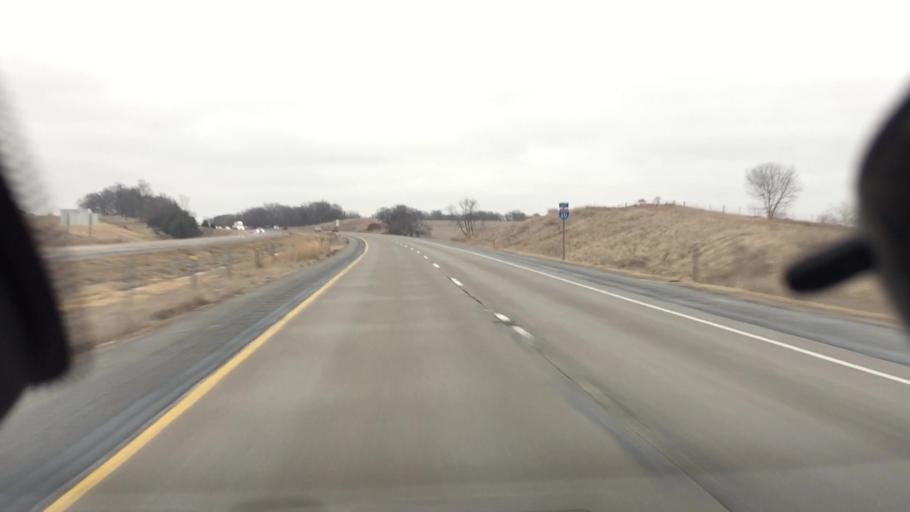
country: US
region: Iowa
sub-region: Cedar County
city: West Branch
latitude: 41.6737
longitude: -91.4380
